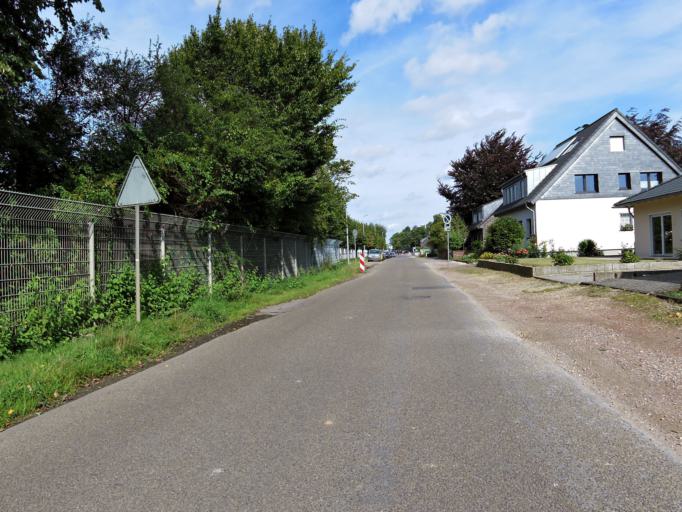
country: DE
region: North Rhine-Westphalia
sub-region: Regierungsbezirk Koln
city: Alsdorf
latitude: 50.8514
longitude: 6.2037
